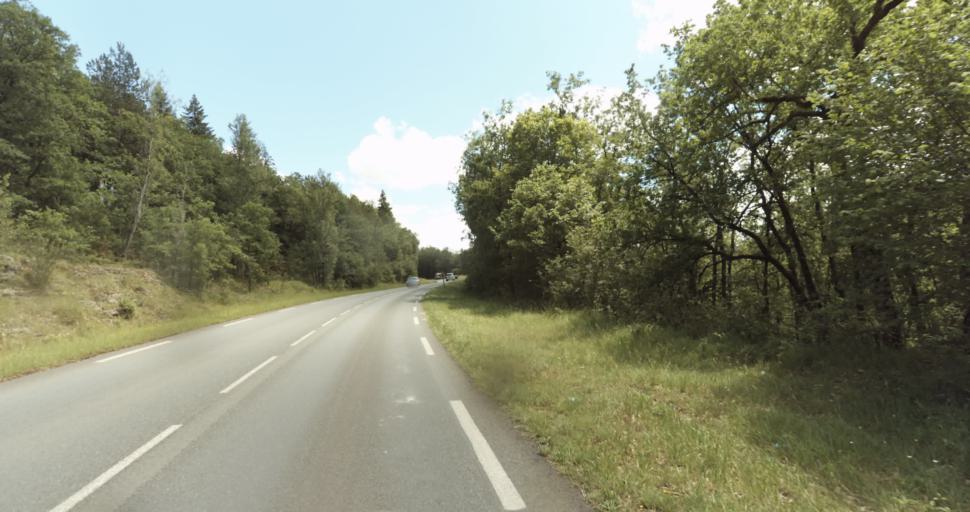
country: FR
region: Aquitaine
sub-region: Departement de la Dordogne
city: Lalinde
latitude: 44.8458
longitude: 0.8234
